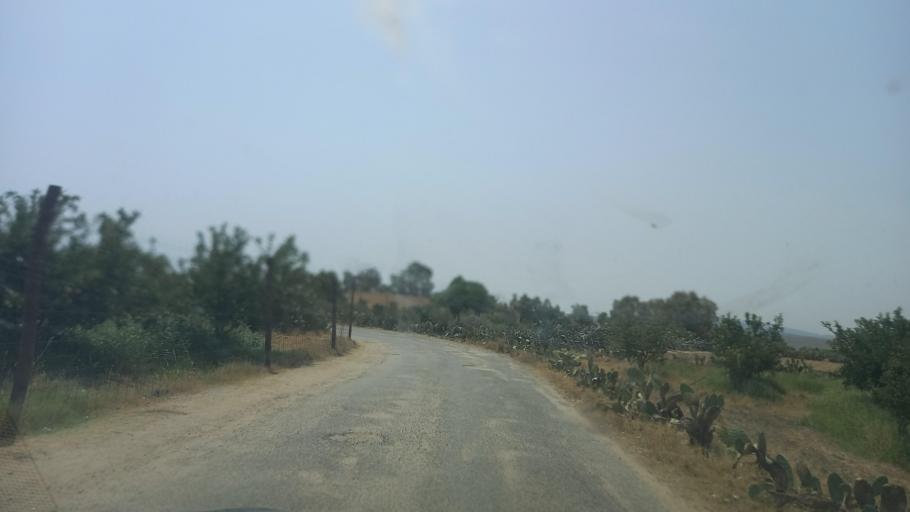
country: TN
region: Al Qasrayn
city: Kasserine
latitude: 35.2479
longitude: 9.0280
